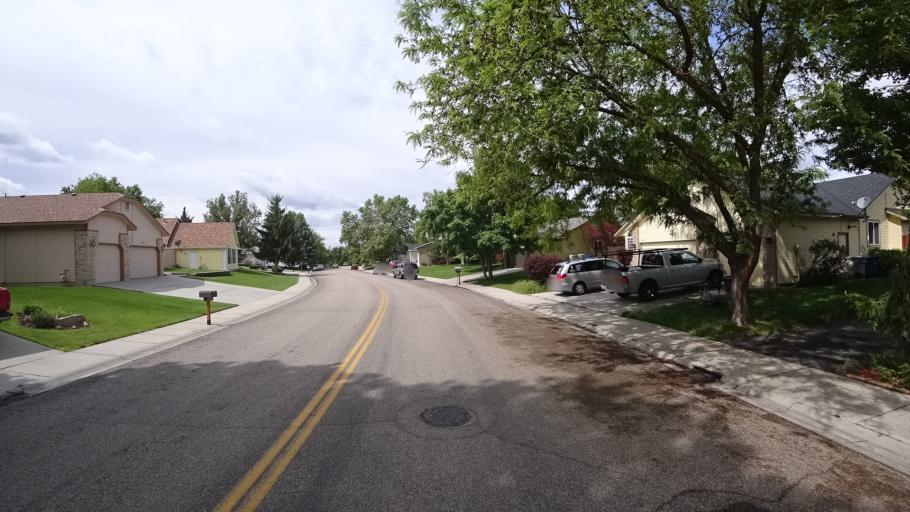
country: US
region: Idaho
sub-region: Ada County
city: Eagle
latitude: 43.7005
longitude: -116.3474
